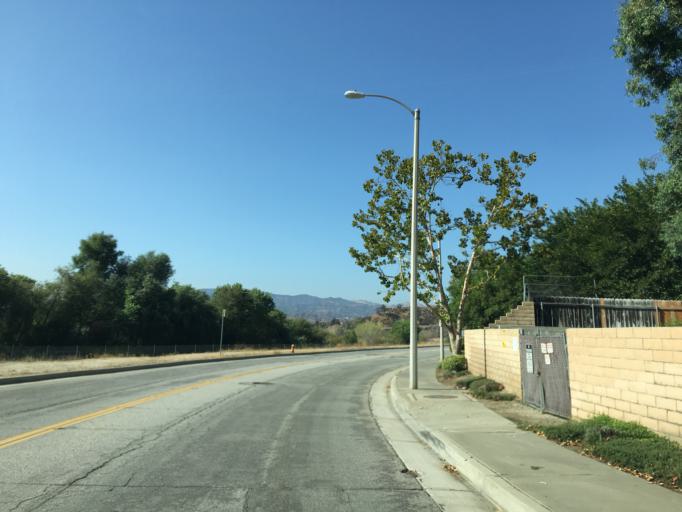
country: US
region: California
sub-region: Los Angeles County
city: Valencia
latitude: 34.4516
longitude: -118.6168
